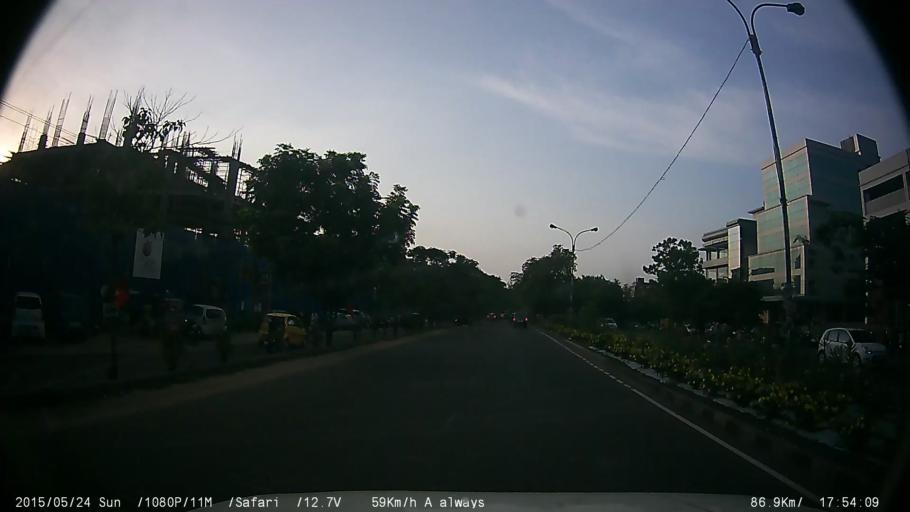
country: IN
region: Kerala
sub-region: Ernakulam
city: Elur
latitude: 10.0141
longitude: 76.3115
